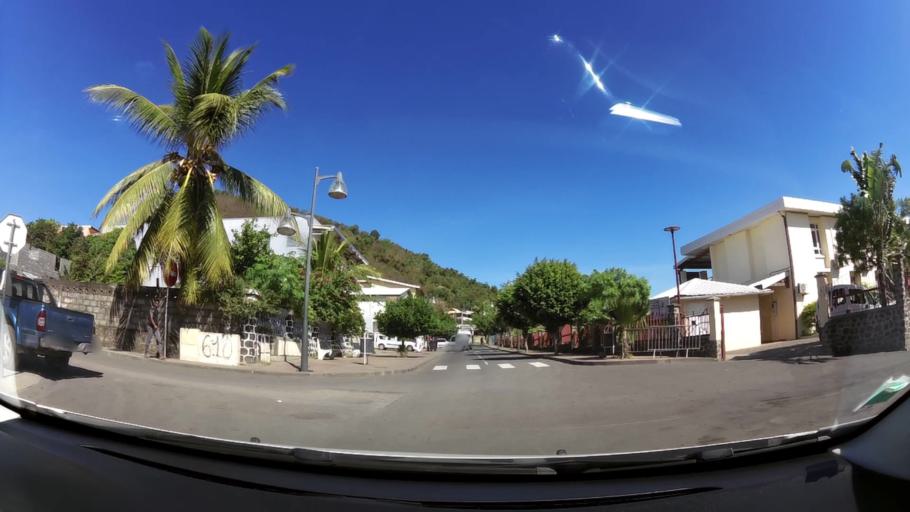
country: YT
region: Pamandzi
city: Pamandzi
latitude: -12.7881
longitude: 45.2728
